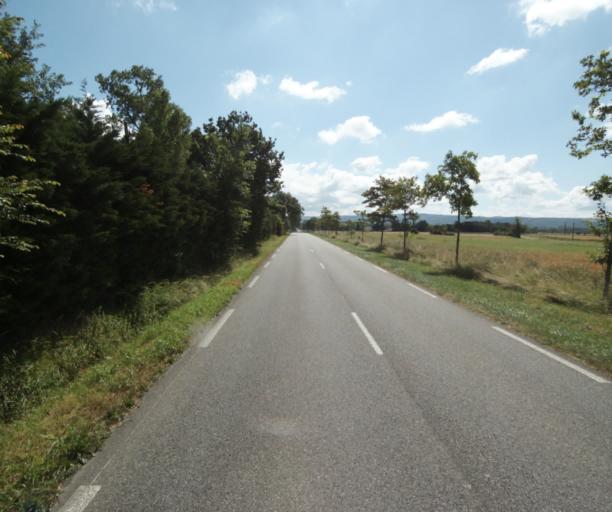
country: FR
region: Midi-Pyrenees
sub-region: Departement de la Haute-Garonne
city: Saint-Felix-Lauragais
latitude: 43.4471
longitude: 1.9346
